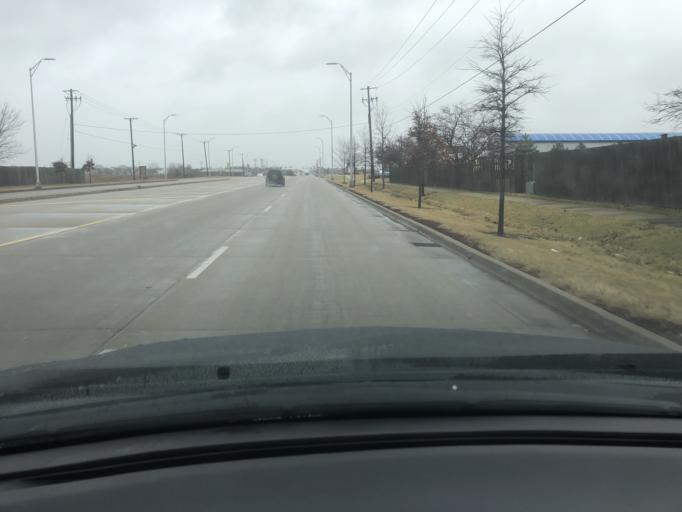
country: US
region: Illinois
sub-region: Will County
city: Shorewood
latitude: 41.5549
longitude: -88.2001
